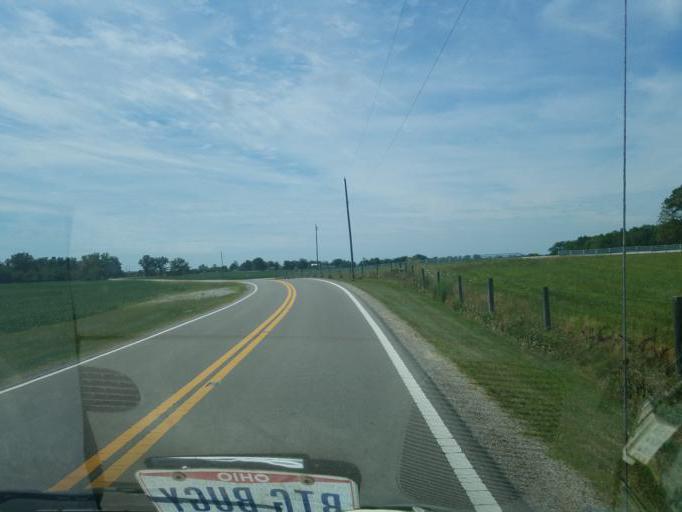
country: US
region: Ohio
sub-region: Madison County
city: Mount Sterling
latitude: 39.8279
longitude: -83.2218
